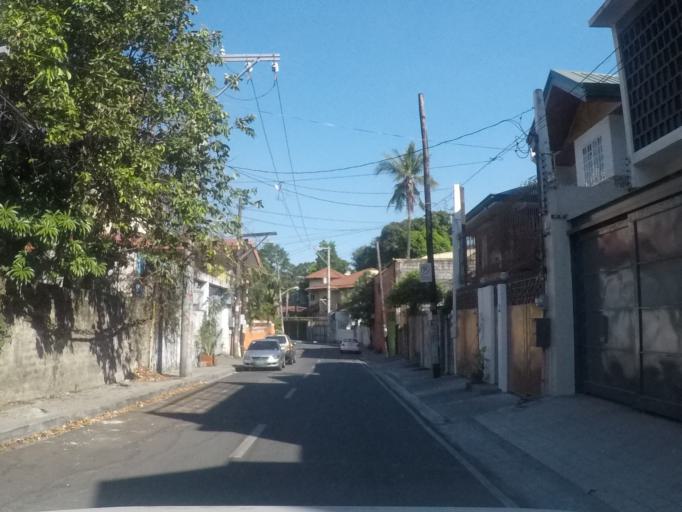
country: PH
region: Metro Manila
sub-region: San Juan
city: San Juan
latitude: 14.6062
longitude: 121.0344
